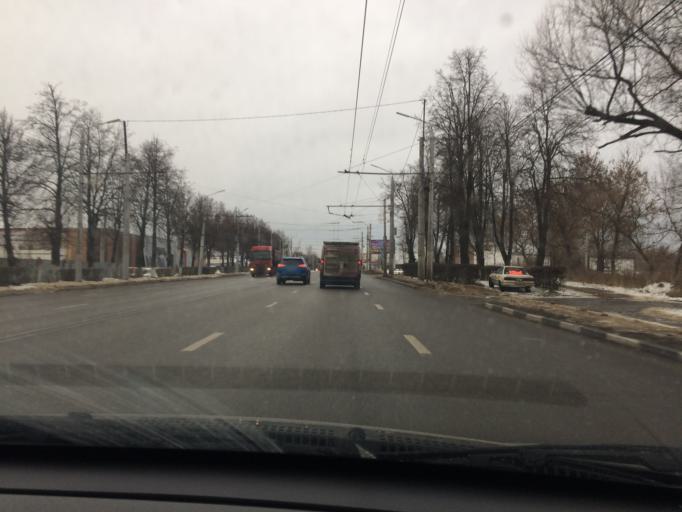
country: RU
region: Tula
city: Gorelki
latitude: 54.2381
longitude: 37.6209
